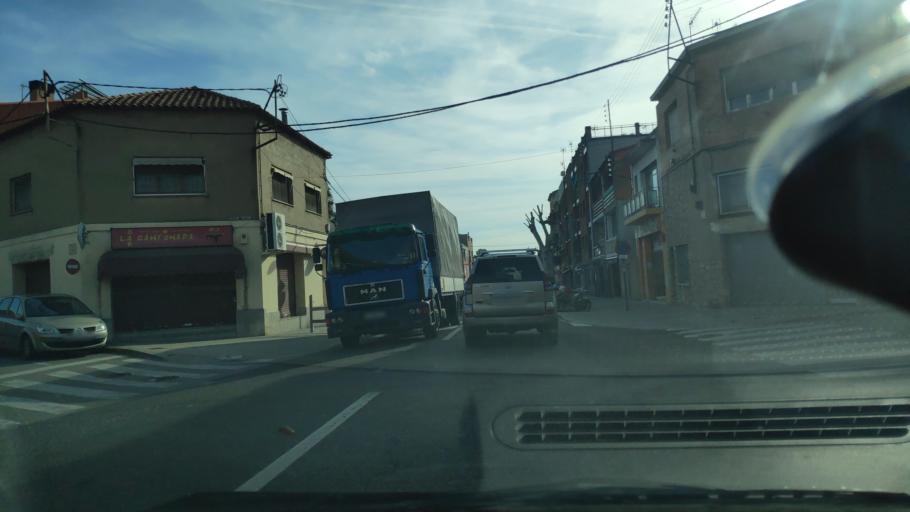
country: ES
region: Catalonia
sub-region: Provincia de Barcelona
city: Castellar del Valles
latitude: 41.6128
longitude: 2.0831
